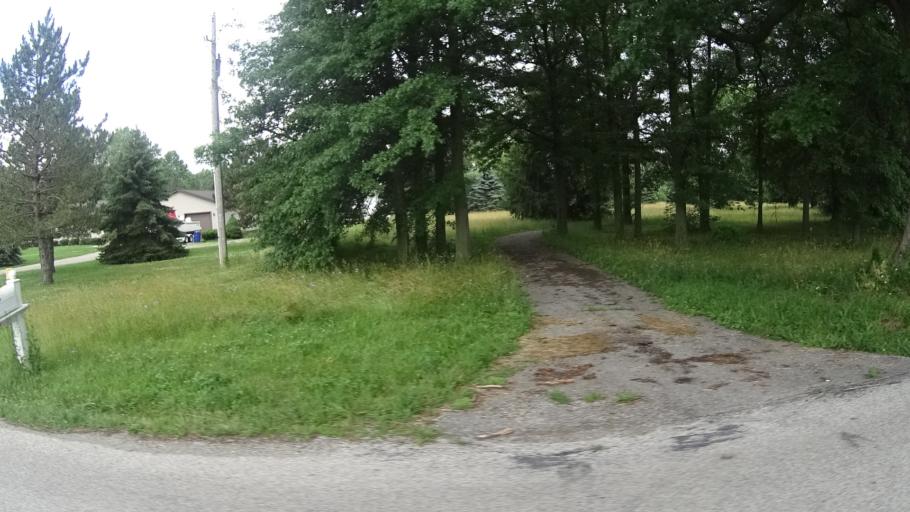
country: US
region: Ohio
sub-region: Huron County
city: Wakeman
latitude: 41.3223
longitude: -82.4663
